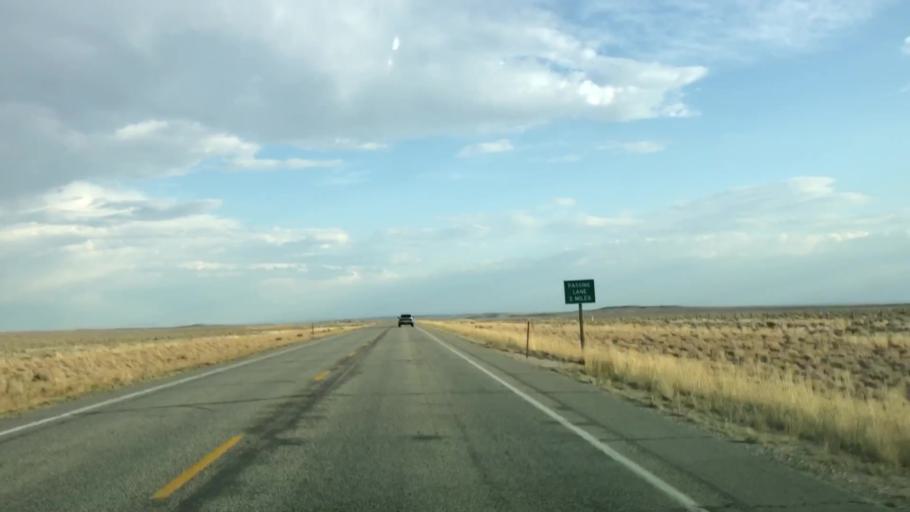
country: US
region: Wyoming
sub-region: Sublette County
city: Pinedale
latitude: 42.3924
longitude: -109.5416
